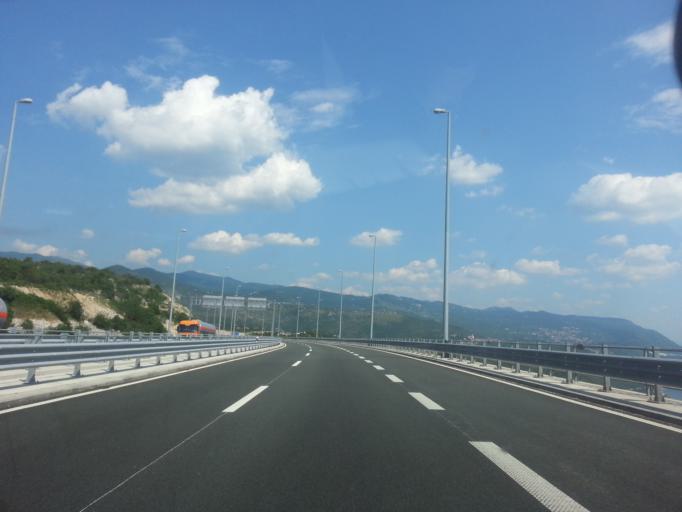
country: HR
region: Primorsko-Goranska
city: Bakar
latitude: 45.3112
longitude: 14.5344
